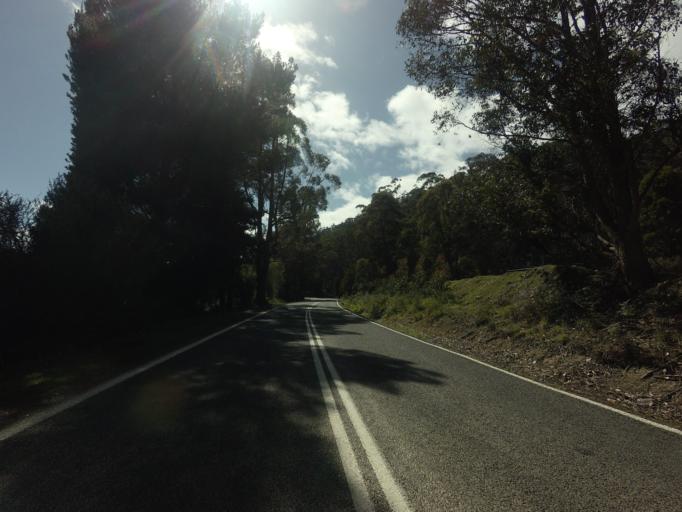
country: AU
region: Tasmania
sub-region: Derwent Valley
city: New Norfolk
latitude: -42.7057
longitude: 146.7119
